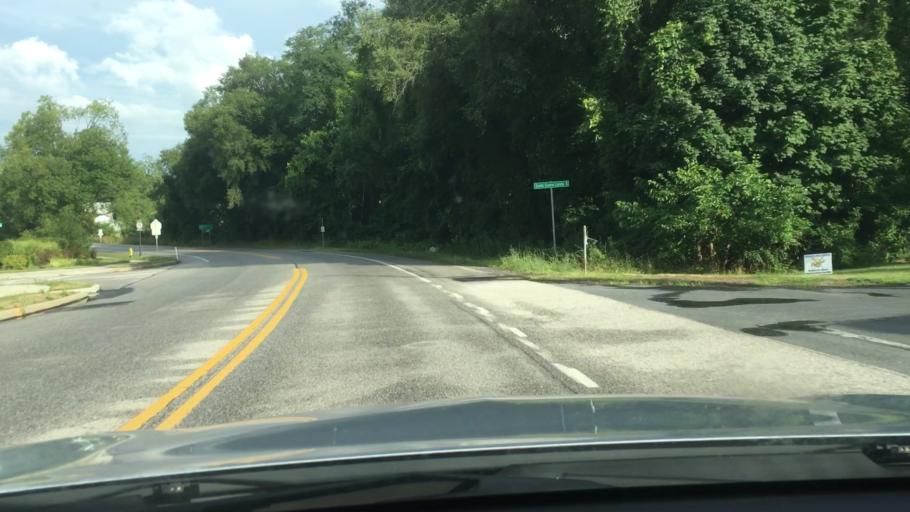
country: US
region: Pennsylvania
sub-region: York County
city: Dillsburg
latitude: 40.1079
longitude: -77.0315
